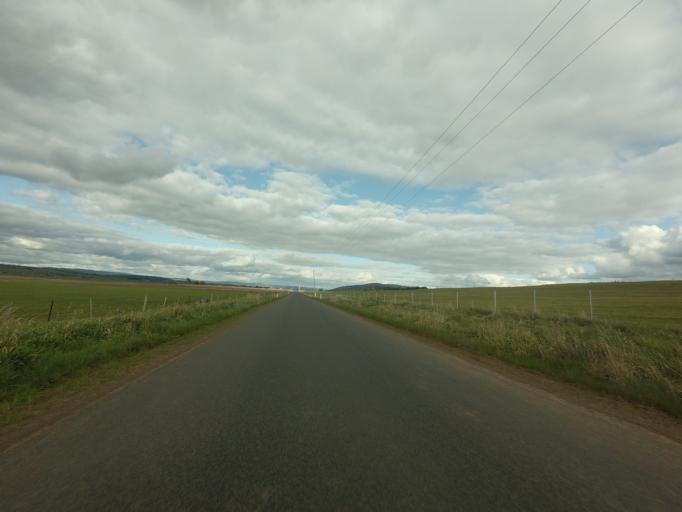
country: AU
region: Tasmania
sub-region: Northern Midlands
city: Evandale
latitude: -41.8898
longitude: 147.3273
